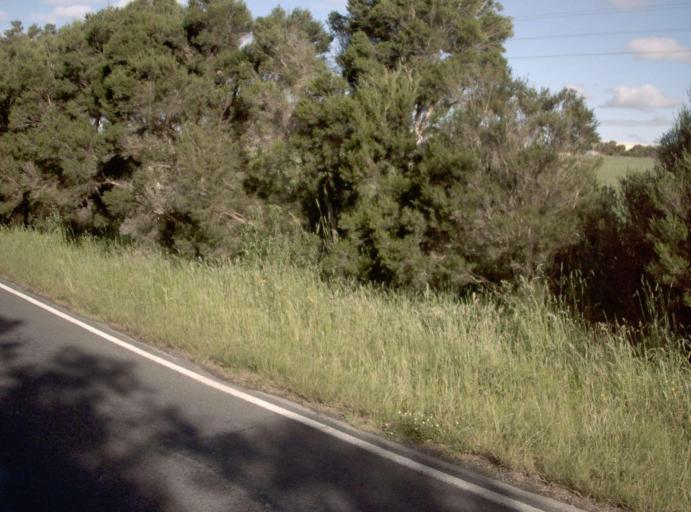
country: AU
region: Victoria
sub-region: Bass Coast
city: North Wonthaggi
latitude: -38.5929
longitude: 145.7945
